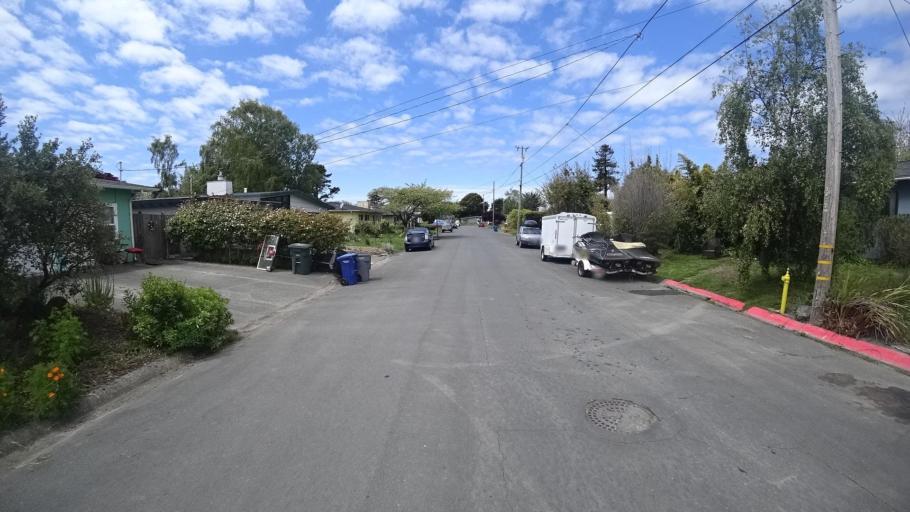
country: US
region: California
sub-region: Humboldt County
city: Arcata
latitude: 40.8852
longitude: -124.0935
